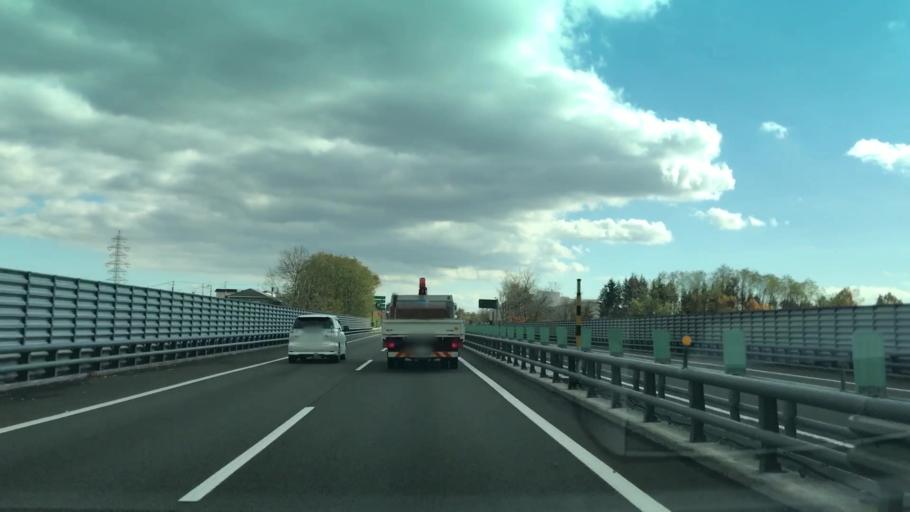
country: JP
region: Hokkaido
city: Kitahiroshima
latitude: 42.9732
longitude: 141.4833
